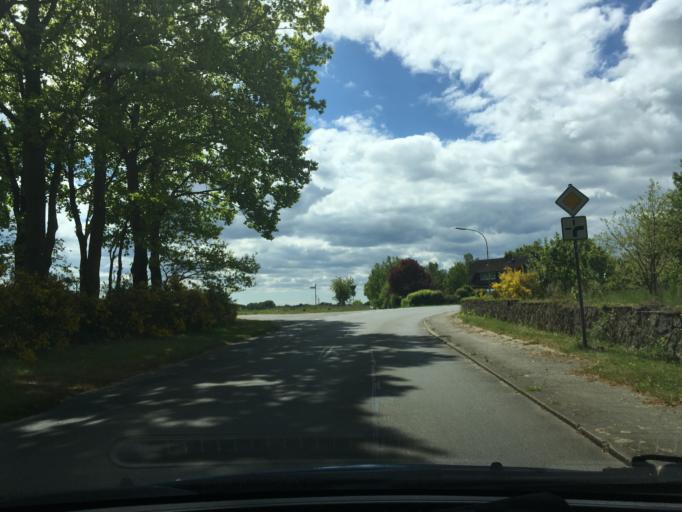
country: DE
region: Lower Saxony
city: Suderburg
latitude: 52.9158
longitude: 10.4586
